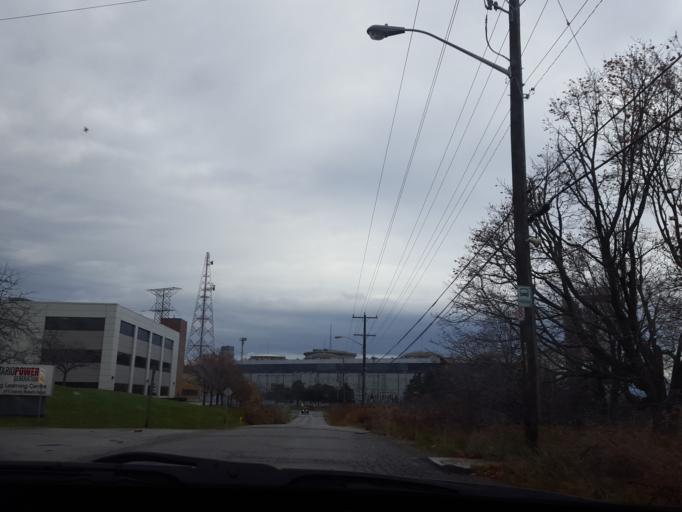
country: CA
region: Ontario
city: Ajax
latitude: 43.8154
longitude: -79.0707
